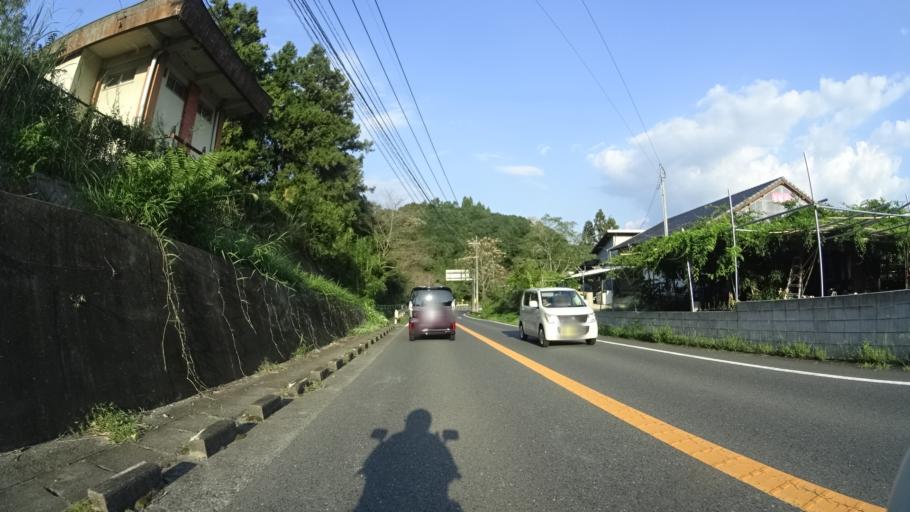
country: JP
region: Oita
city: Bungo-Takada-shi
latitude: 33.4433
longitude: 131.3487
